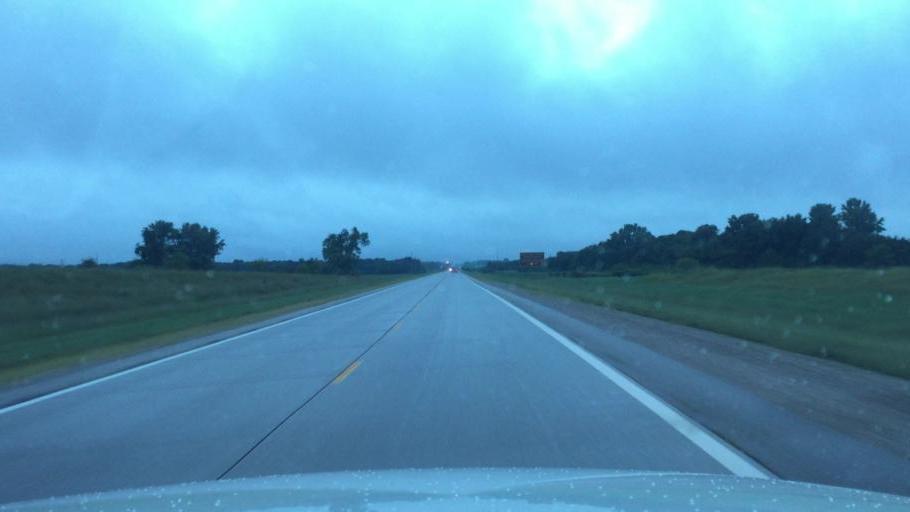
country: US
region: Kansas
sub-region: Neosho County
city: Chanute
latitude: 37.7133
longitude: -95.4790
